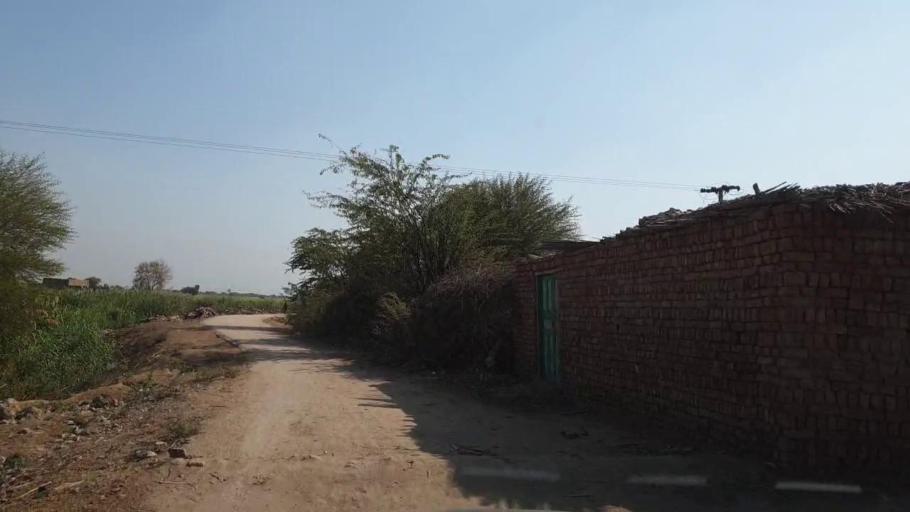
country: PK
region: Sindh
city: Tando Allahyar
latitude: 25.5852
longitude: 68.7524
